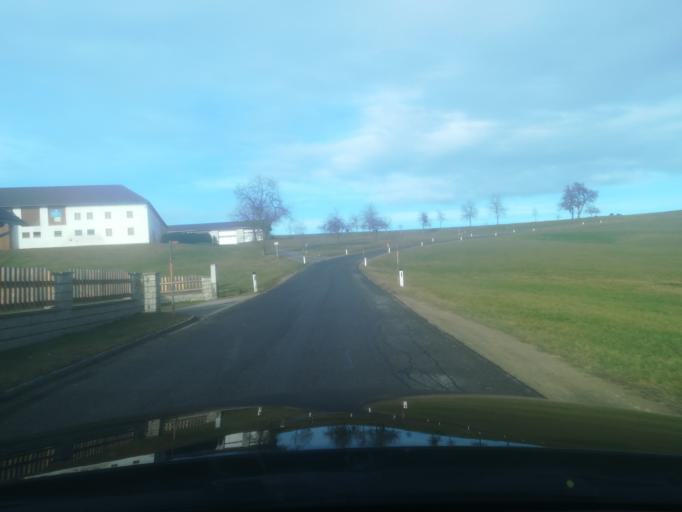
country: AT
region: Upper Austria
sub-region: Politischer Bezirk Perg
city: Perg
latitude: 48.3571
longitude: 14.6250
